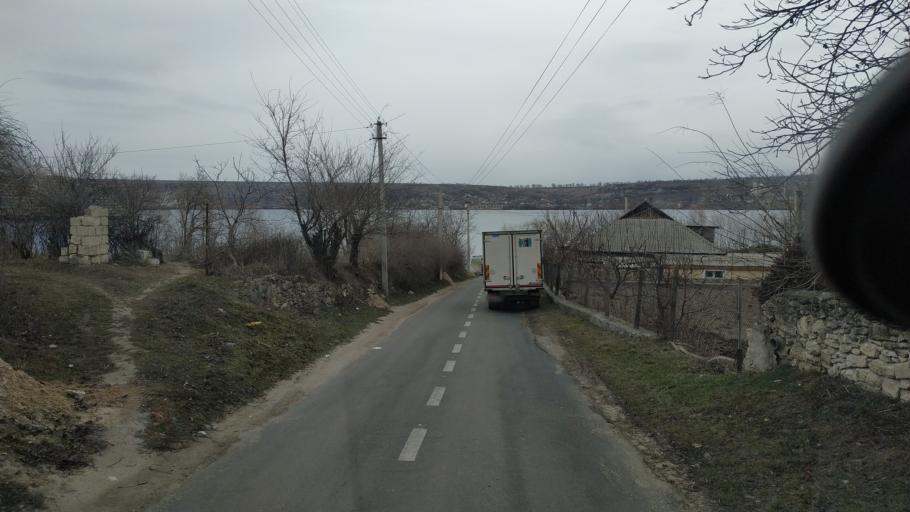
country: MD
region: Telenesti
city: Cocieri
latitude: 47.3492
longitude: 29.0918
